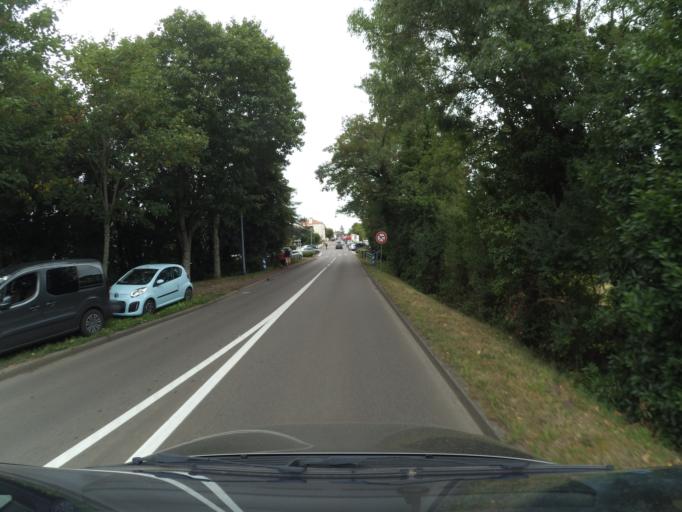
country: FR
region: Pays de la Loire
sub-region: Departement de la Vendee
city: Moutiers-les-Mauxfaits
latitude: 46.4913
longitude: -1.4327
